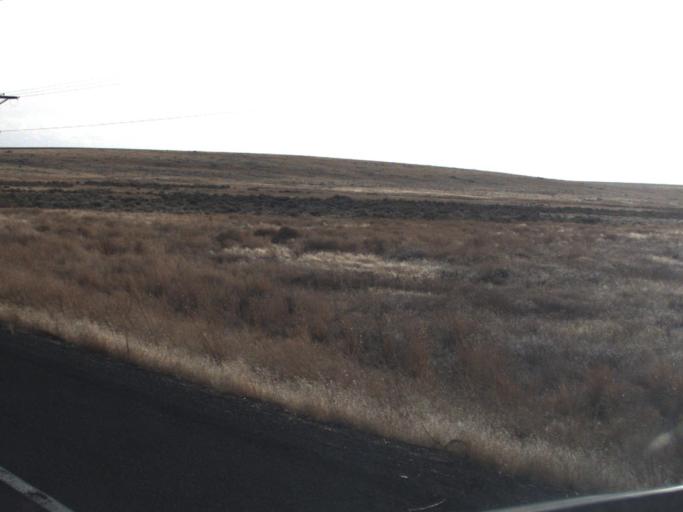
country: US
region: Washington
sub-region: Adams County
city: Ritzville
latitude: 47.2285
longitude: -118.6863
